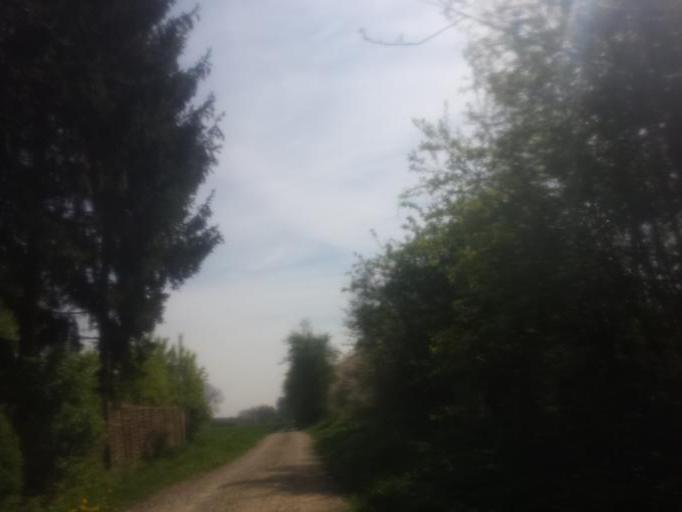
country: DE
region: Bavaria
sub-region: Upper Bavaria
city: Manching
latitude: 48.7283
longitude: 11.4568
